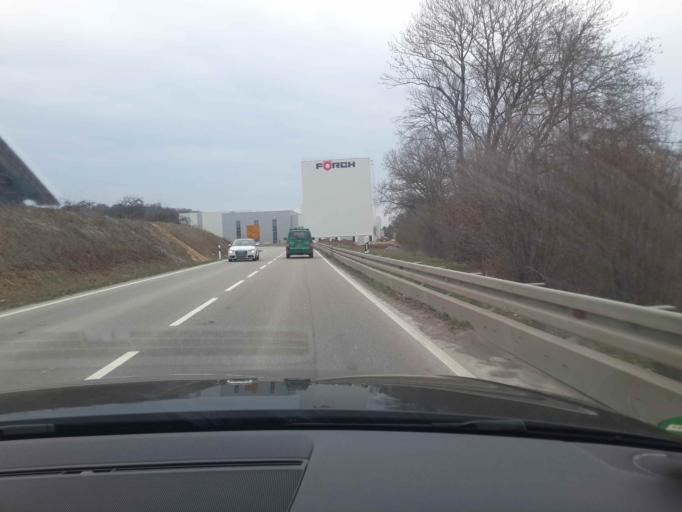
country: DE
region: Baden-Wuerttemberg
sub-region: Regierungsbezirk Stuttgart
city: Neuenstadt am Kocher
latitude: 49.2389
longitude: 9.3131
